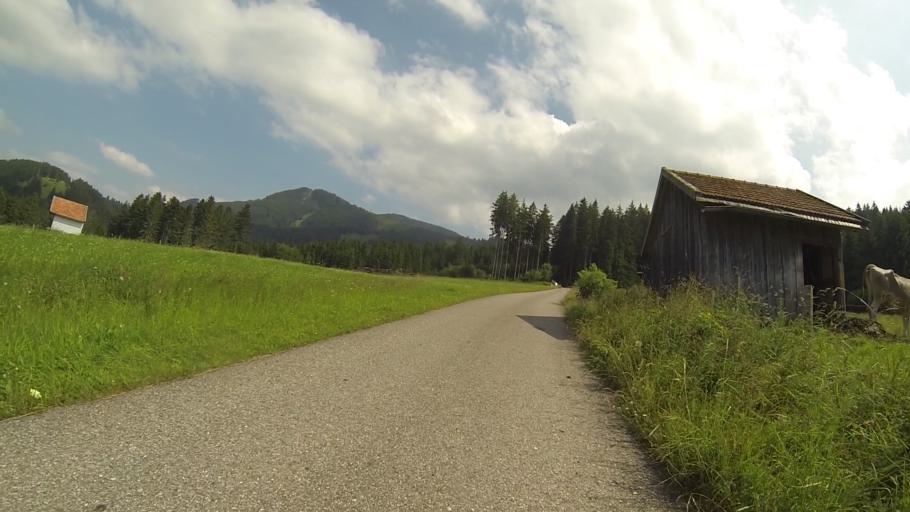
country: DE
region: Bavaria
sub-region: Swabia
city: Nesselwang
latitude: 47.6080
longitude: 10.4700
